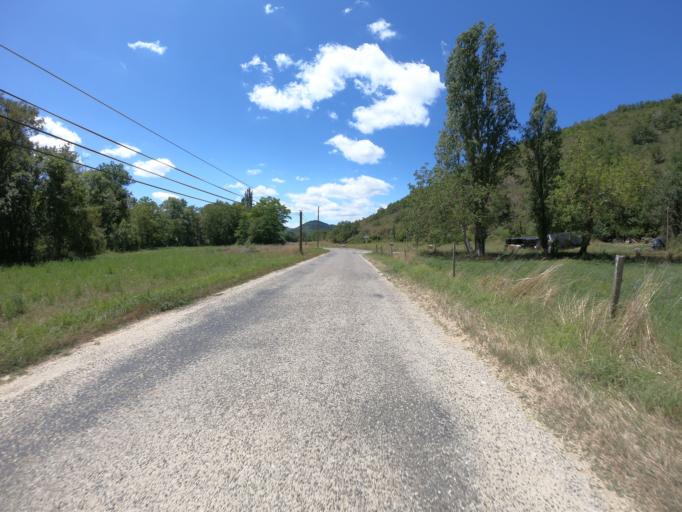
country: FR
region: Midi-Pyrenees
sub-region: Departement de l'Ariege
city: Mirepoix
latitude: 43.0496
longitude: 1.7986
